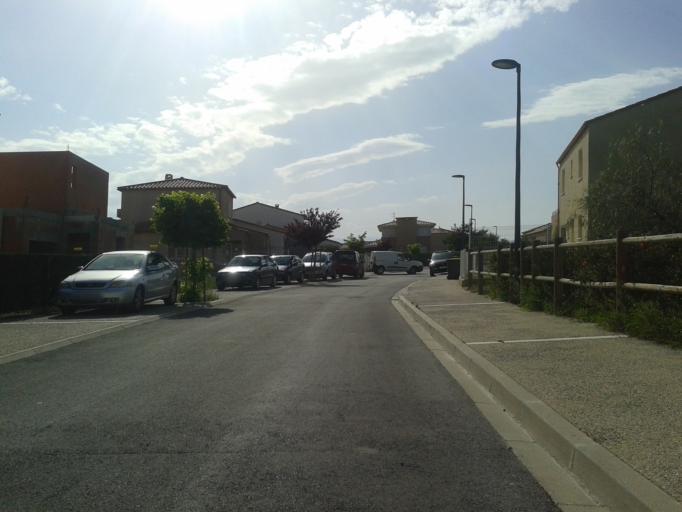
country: FR
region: Languedoc-Roussillon
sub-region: Departement des Pyrenees-Orientales
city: Pezilla-la-Riviere
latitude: 42.6941
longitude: 2.7794
